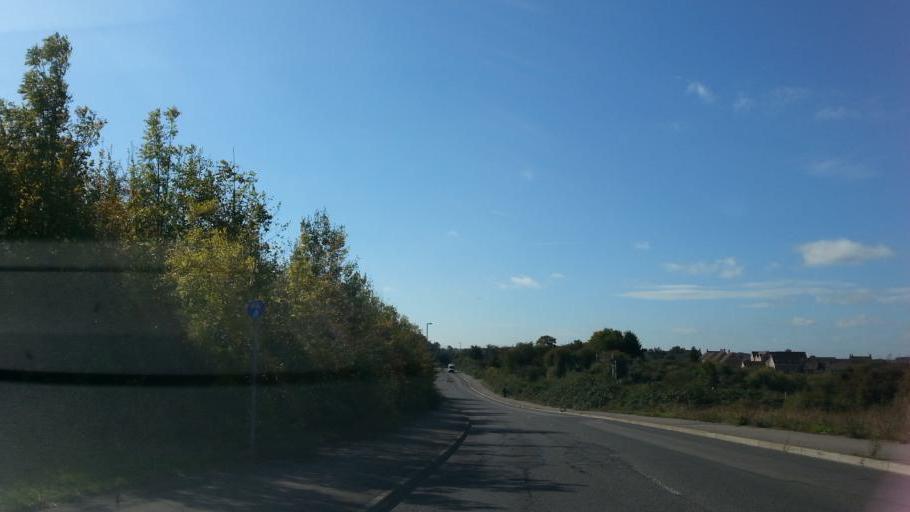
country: GB
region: England
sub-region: Northamptonshire
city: Higham Ferrers
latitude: 52.2985
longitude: -0.5906
